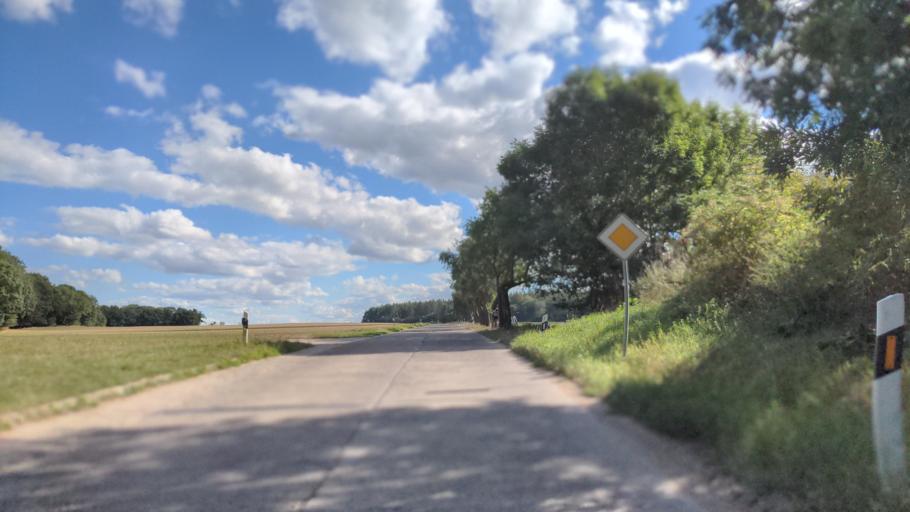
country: DE
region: Mecklenburg-Vorpommern
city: Gramkow
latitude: 53.9213
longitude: 11.3719
